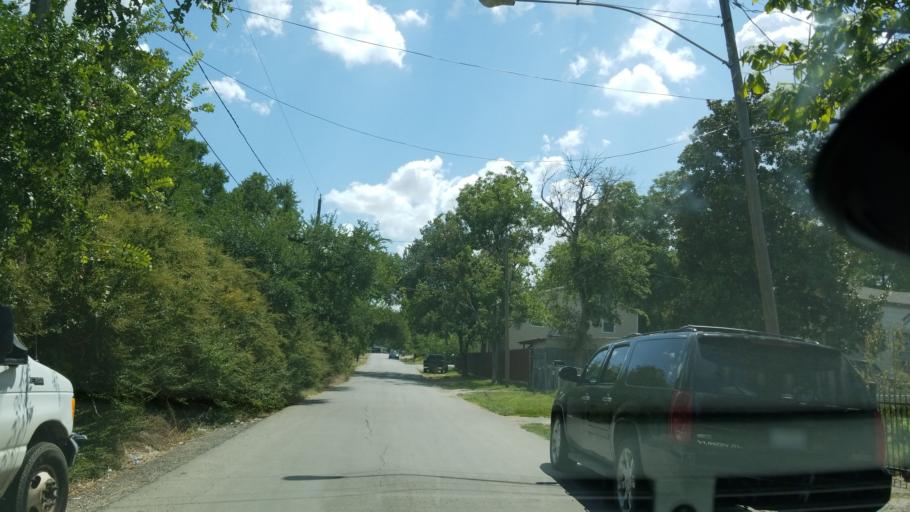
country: US
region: Texas
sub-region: Dallas County
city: Cockrell Hill
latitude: 32.7477
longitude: -96.9062
